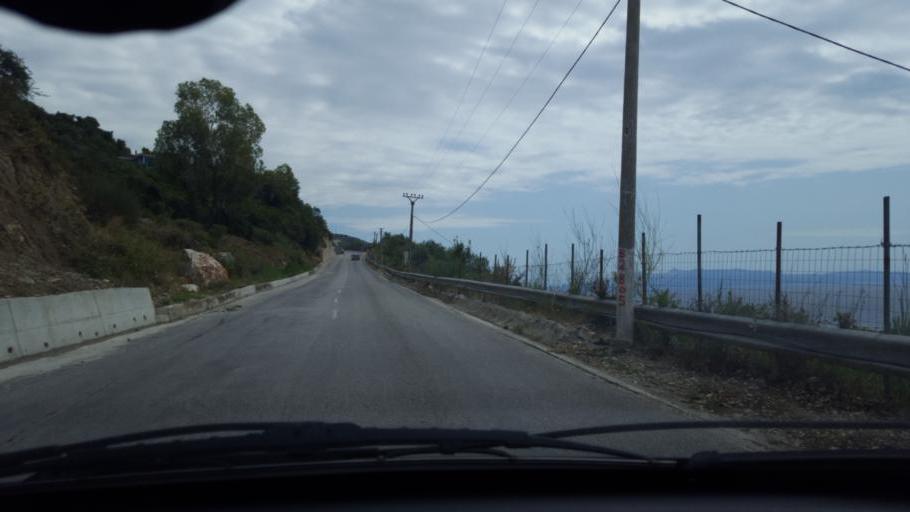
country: AL
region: Vlore
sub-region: Rrethi i Sarandes
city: Lukove
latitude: 40.0601
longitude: 19.8585
